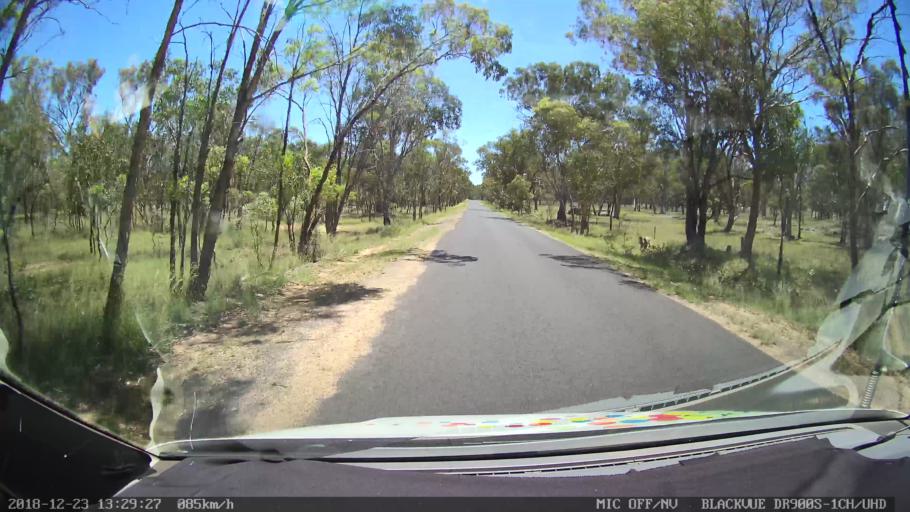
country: AU
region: New South Wales
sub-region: Armidale Dumaresq
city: Armidale
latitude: -30.4638
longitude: 151.3350
